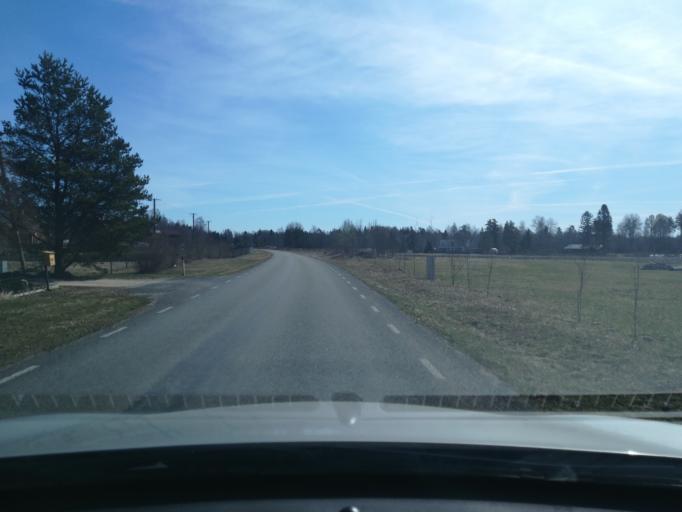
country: EE
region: Harju
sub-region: Saue linn
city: Saue
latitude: 59.3000
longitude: 24.5933
